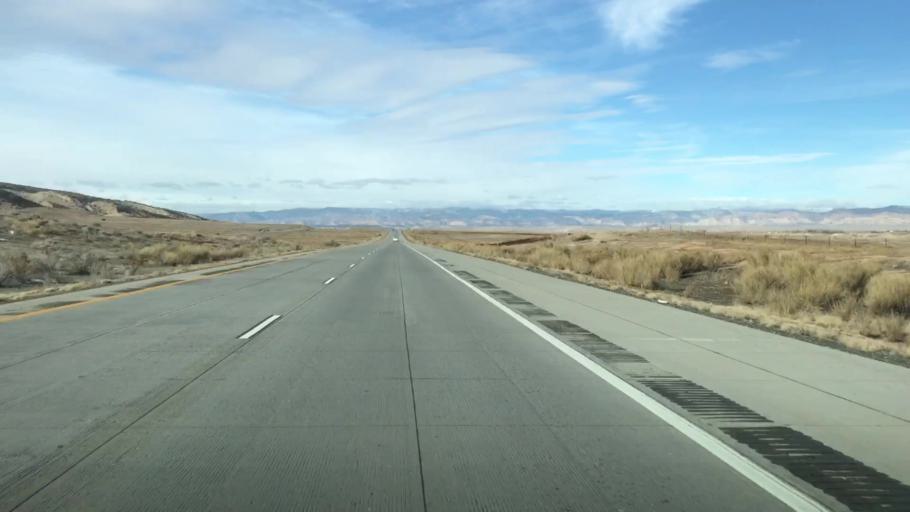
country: US
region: Colorado
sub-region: Mesa County
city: Loma
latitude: 39.1957
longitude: -108.8444
